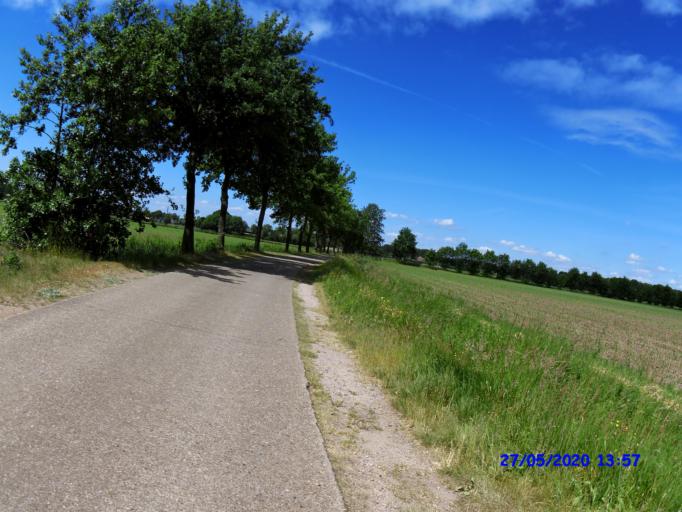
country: BE
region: Flanders
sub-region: Provincie Antwerpen
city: Kasterlee
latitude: 51.2380
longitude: 4.9117
